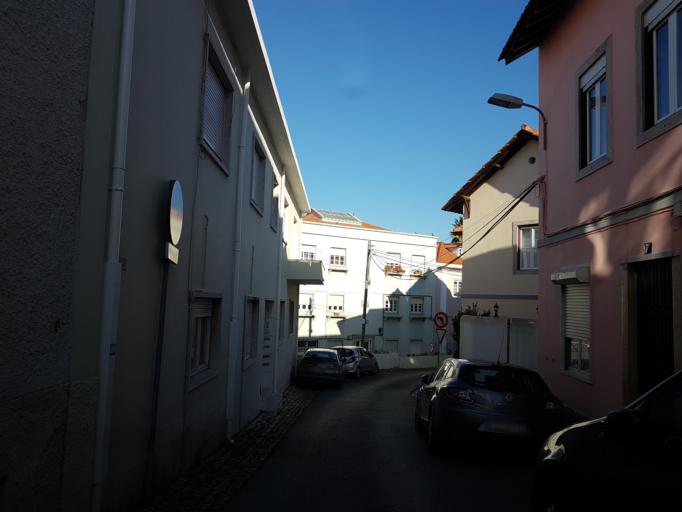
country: PT
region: Lisbon
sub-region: Sintra
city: Sintra
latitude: 38.7983
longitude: -9.3855
